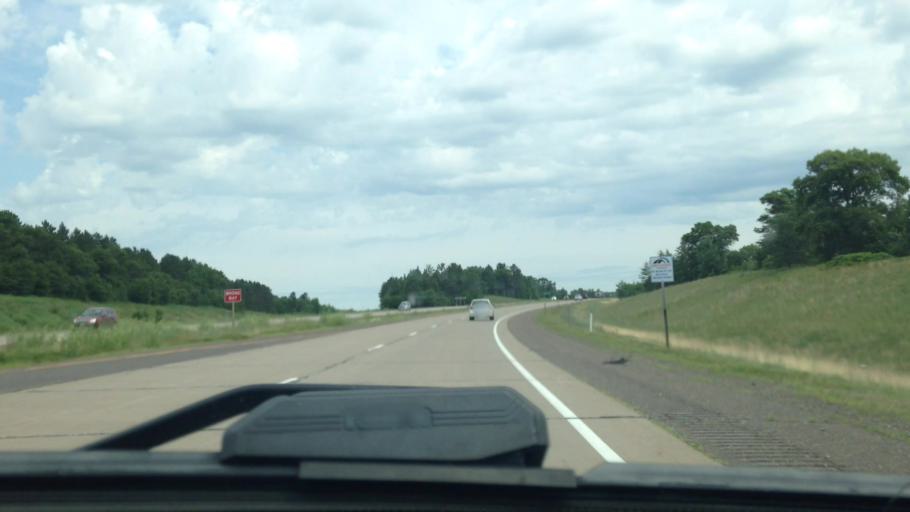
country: US
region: Wisconsin
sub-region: Douglas County
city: Lake Nebagamon
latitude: 46.2034
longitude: -91.7994
